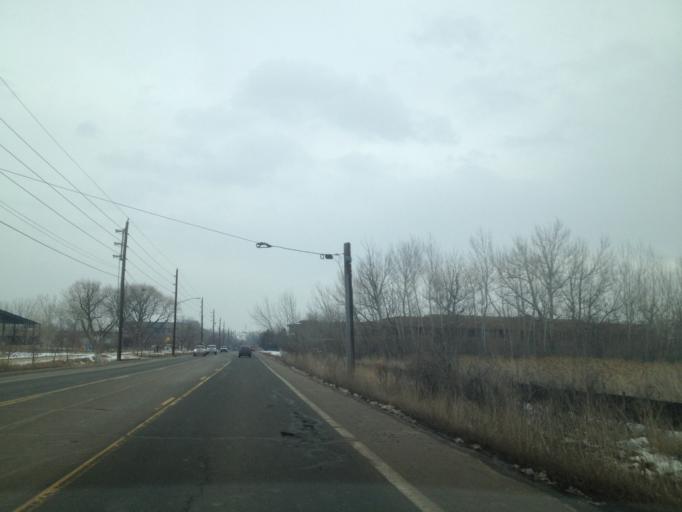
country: US
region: Colorado
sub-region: Boulder County
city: Boulder
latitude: 40.0292
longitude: -105.2315
